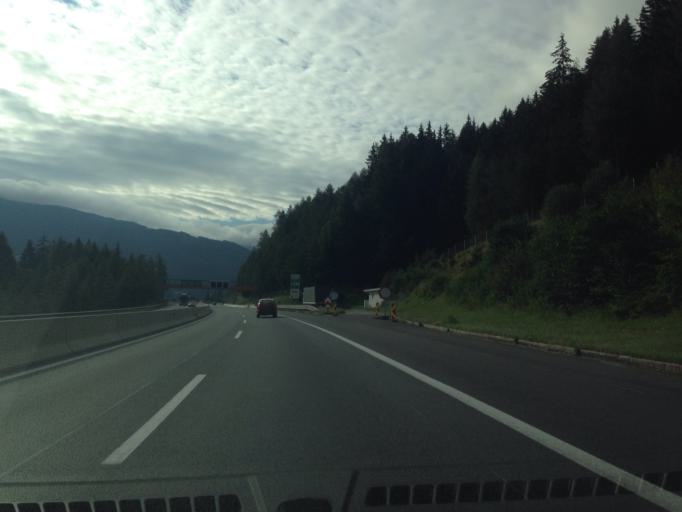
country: AT
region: Tyrol
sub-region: Politischer Bezirk Innsbruck Land
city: Ellbogen
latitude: 47.1608
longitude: 11.4356
